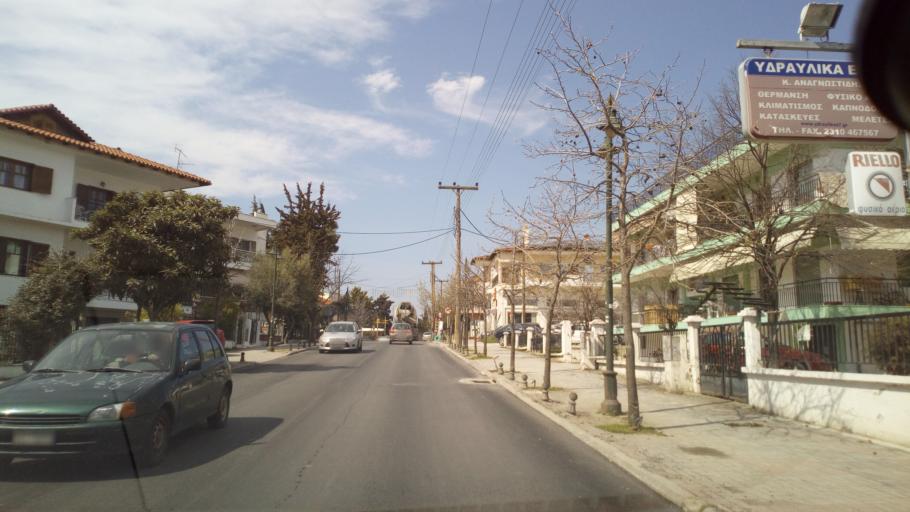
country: GR
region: Central Macedonia
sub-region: Nomos Thessalonikis
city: Thermi
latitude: 40.5479
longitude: 23.0251
